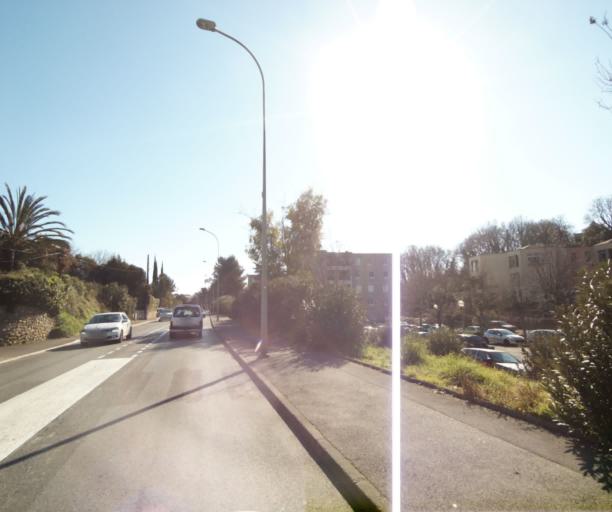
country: FR
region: Provence-Alpes-Cote d'Azur
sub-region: Departement des Alpes-Maritimes
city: Biot
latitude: 43.5989
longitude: 7.1016
